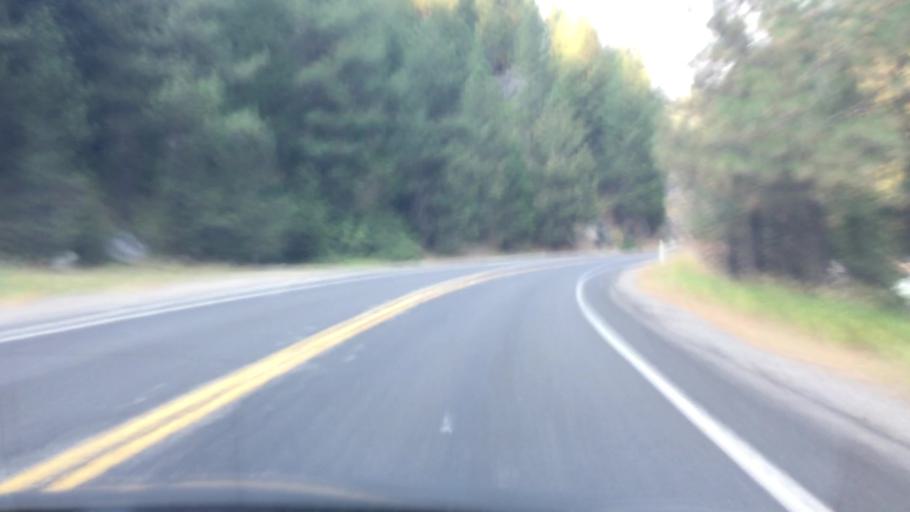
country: US
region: Idaho
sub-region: Valley County
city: Cascade
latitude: 44.2540
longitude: -116.0857
